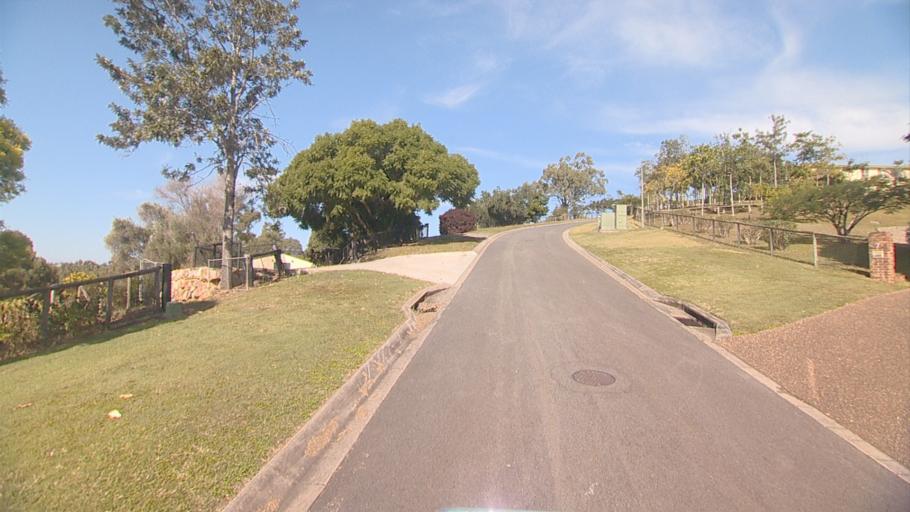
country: AU
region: Queensland
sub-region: Logan
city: Windaroo
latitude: -27.7578
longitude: 153.1763
